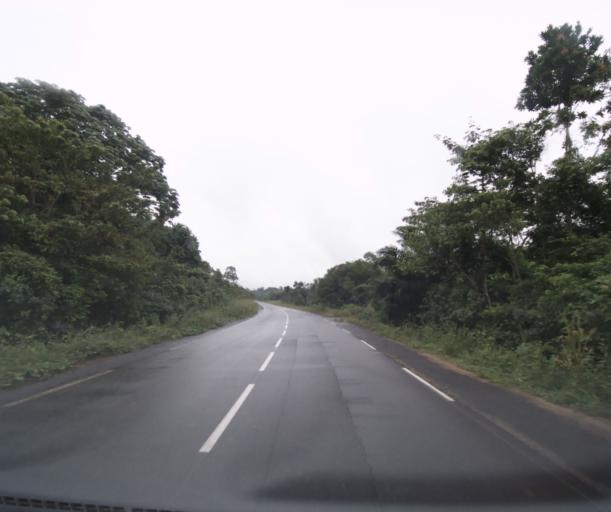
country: CM
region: Littoral
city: Dizangue
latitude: 3.3819
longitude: 10.1039
